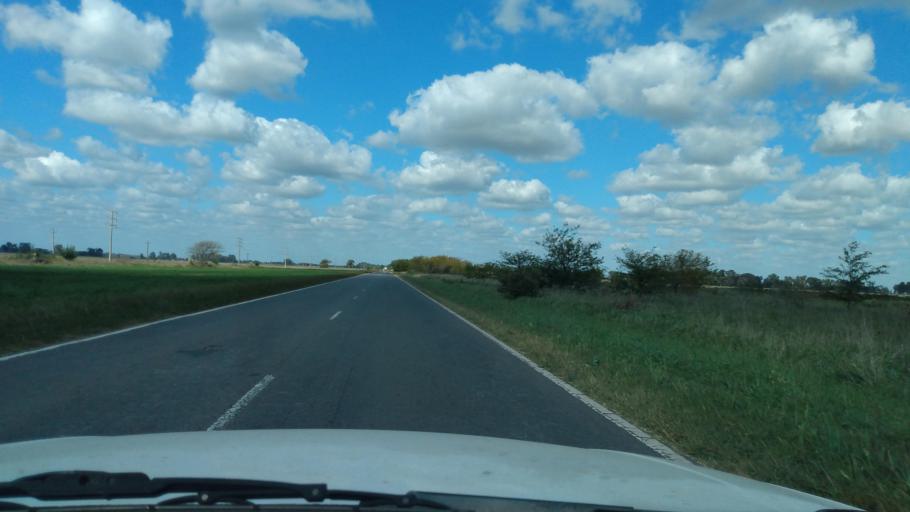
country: AR
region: Buenos Aires
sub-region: Partido de Navarro
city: Navarro
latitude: -34.9074
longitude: -59.3323
